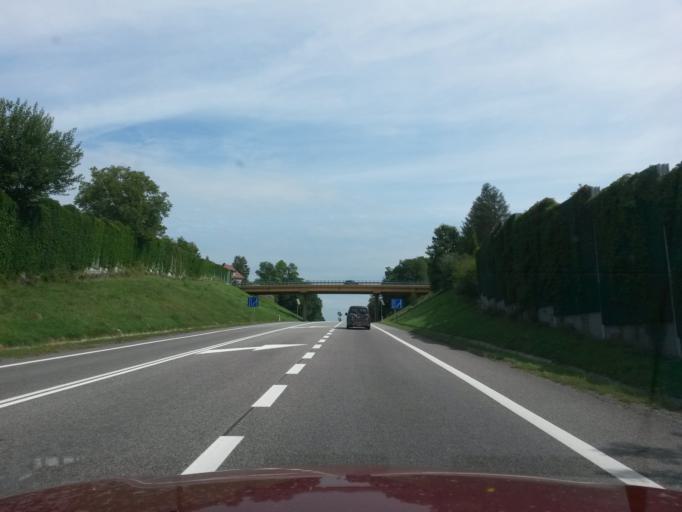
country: PL
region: Lesser Poland Voivodeship
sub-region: Powiat bochenski
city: Bochnia
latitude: 49.9600
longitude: 20.4369
